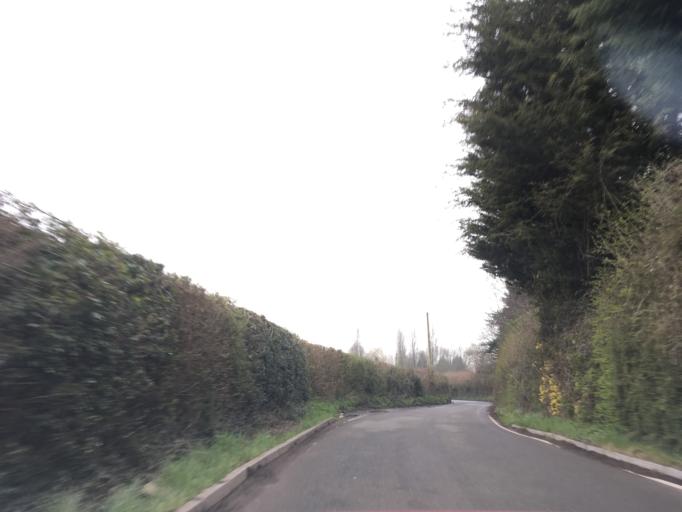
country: GB
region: Wales
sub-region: Newport
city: Marshfield
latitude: 51.5462
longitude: -3.0482
